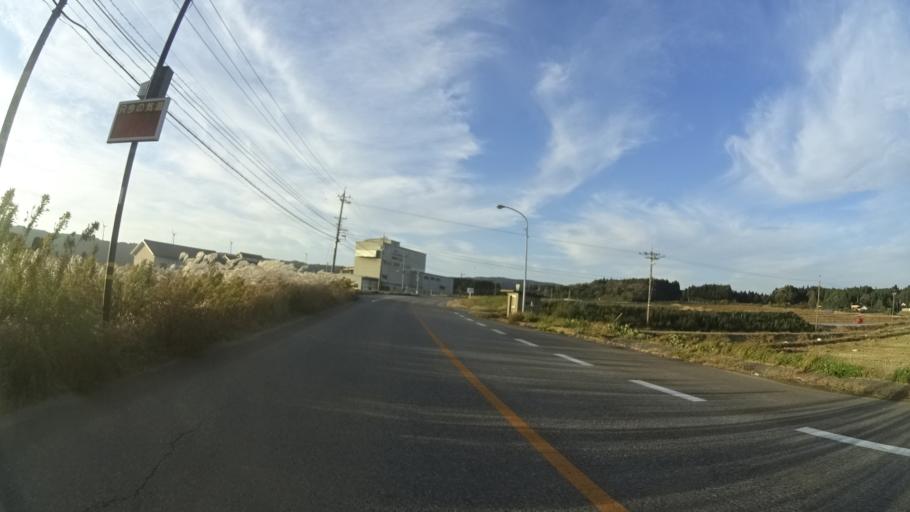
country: JP
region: Ishikawa
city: Nanao
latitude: 37.1588
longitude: 136.7174
